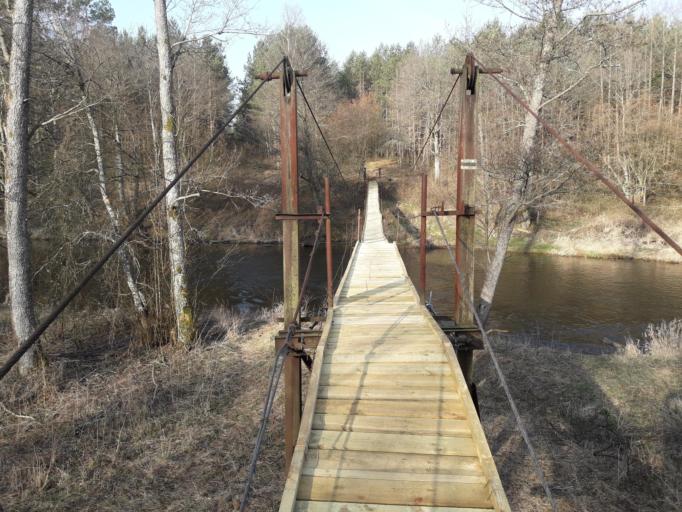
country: LT
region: Alytaus apskritis
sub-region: Alytaus rajonas
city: Daugai
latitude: 54.1156
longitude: 24.2564
